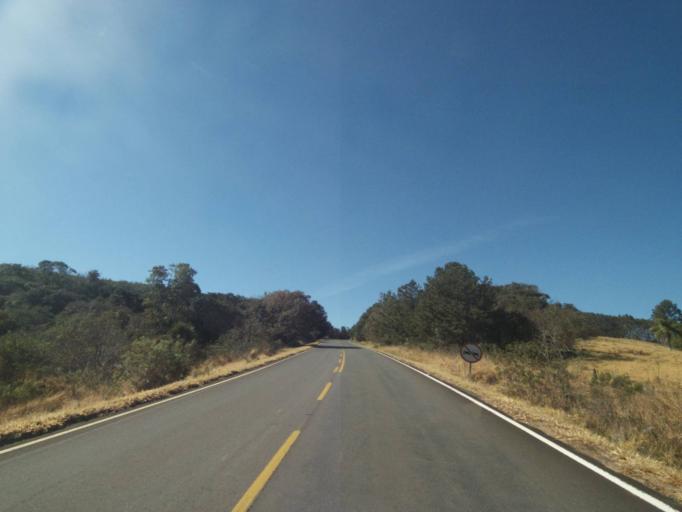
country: BR
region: Parana
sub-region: Tibagi
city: Tibagi
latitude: -24.4725
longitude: -50.5278
